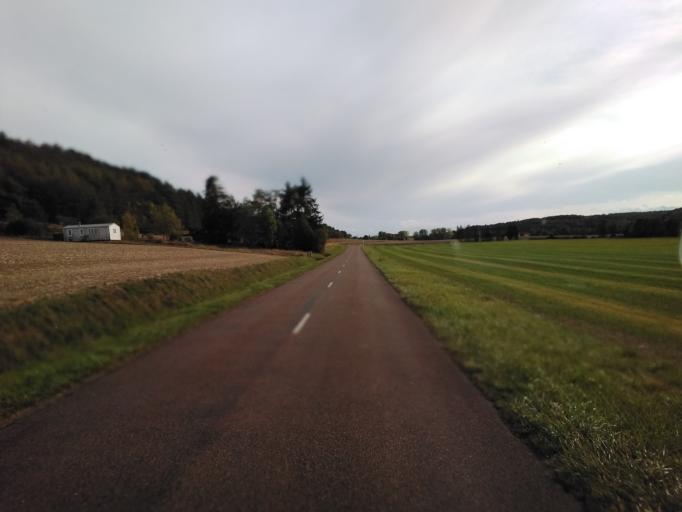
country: FR
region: Champagne-Ardenne
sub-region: Departement de l'Aube
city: Les Riceys
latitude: 47.9100
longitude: 4.3642
